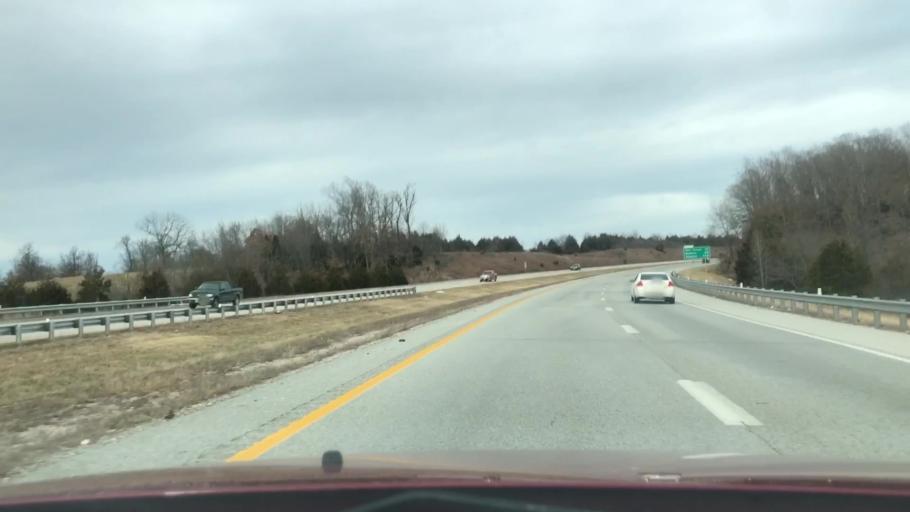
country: US
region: Missouri
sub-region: Greene County
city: Springfield
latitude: 37.2645
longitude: -93.2243
